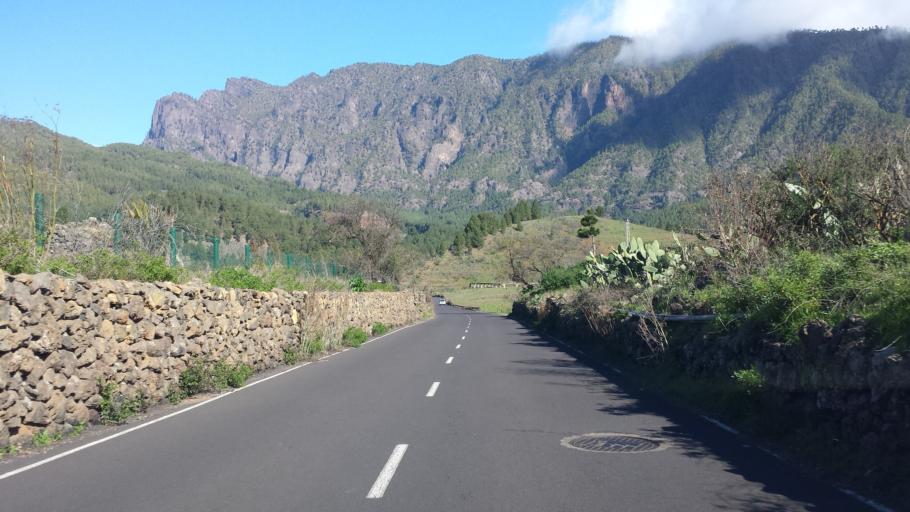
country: ES
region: Canary Islands
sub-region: Provincia de Santa Cruz de Tenerife
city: El Paso
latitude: 28.6559
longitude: -17.8526
